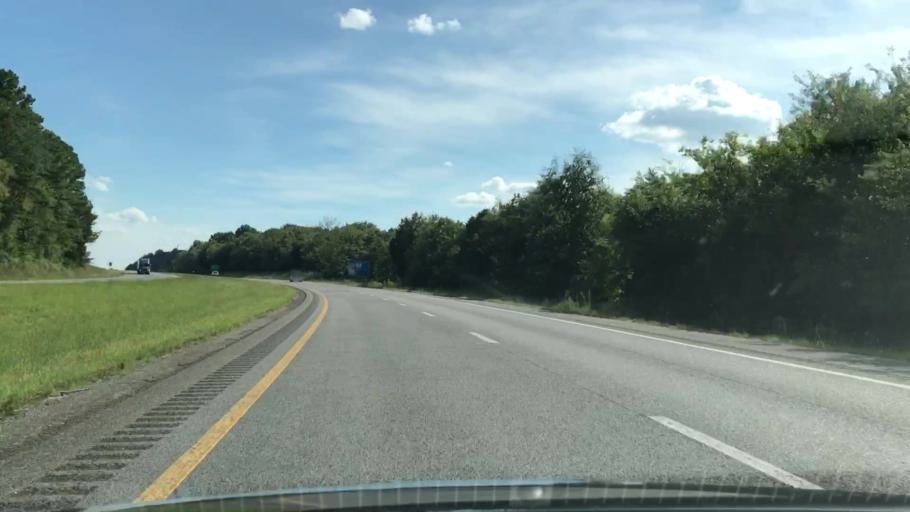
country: US
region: Alabama
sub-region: Limestone County
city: Ardmore
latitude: 35.1057
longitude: -86.8857
